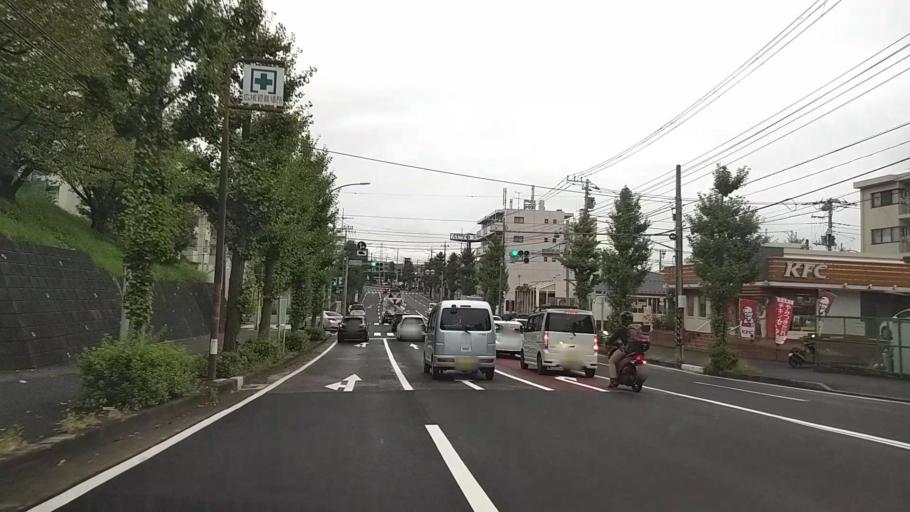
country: JP
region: Kanagawa
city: Kamakura
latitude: 35.3960
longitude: 139.5650
